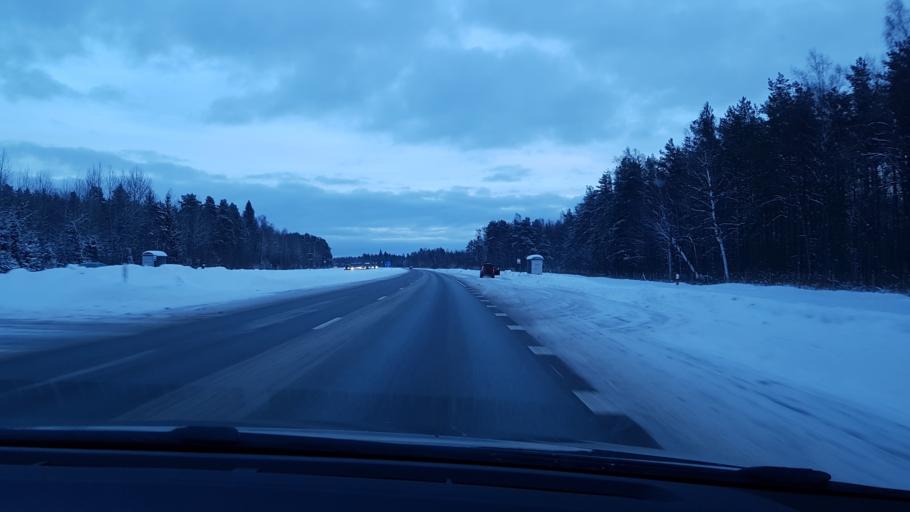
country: EE
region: Harju
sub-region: Raasiku vald
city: Raasiku
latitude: 59.4358
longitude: 25.1638
